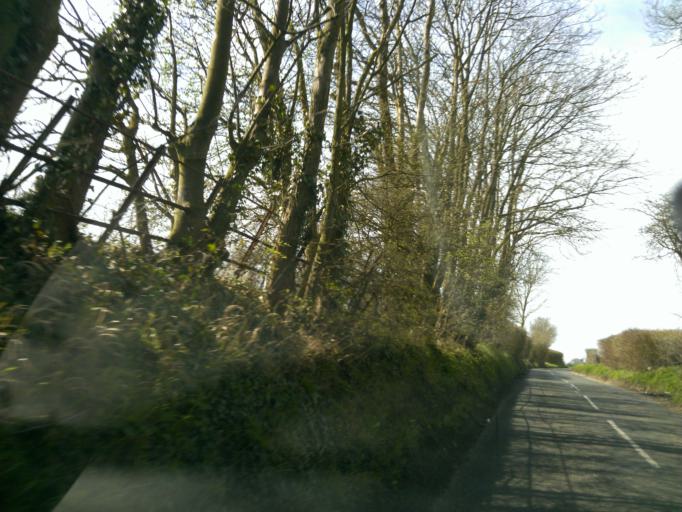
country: GB
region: England
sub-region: Essex
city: Kelvedon
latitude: 51.8382
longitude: 0.6774
